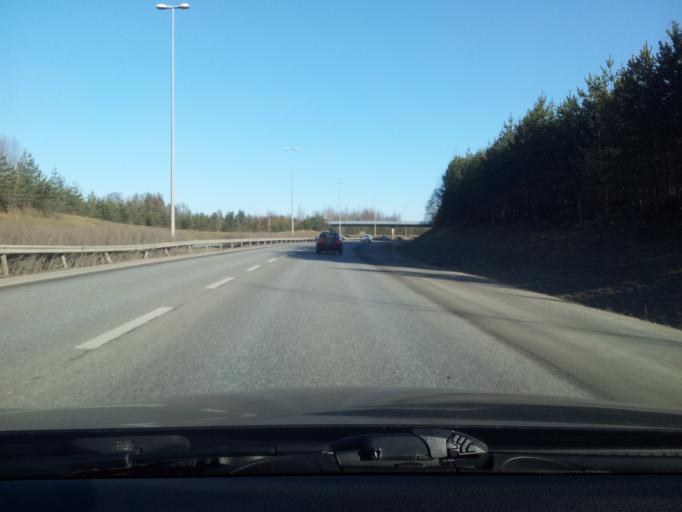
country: FI
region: Uusimaa
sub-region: Helsinki
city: Kauniainen
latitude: 60.1954
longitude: 24.7435
